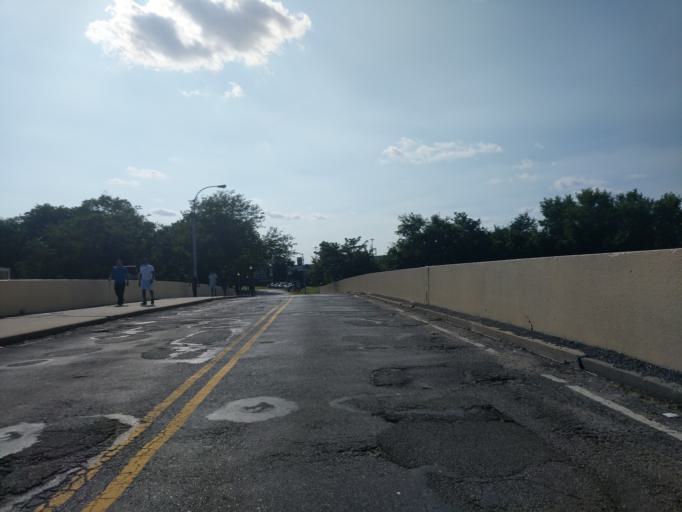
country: US
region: New York
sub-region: Queens County
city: Jamaica
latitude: 40.7527
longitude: -73.8398
